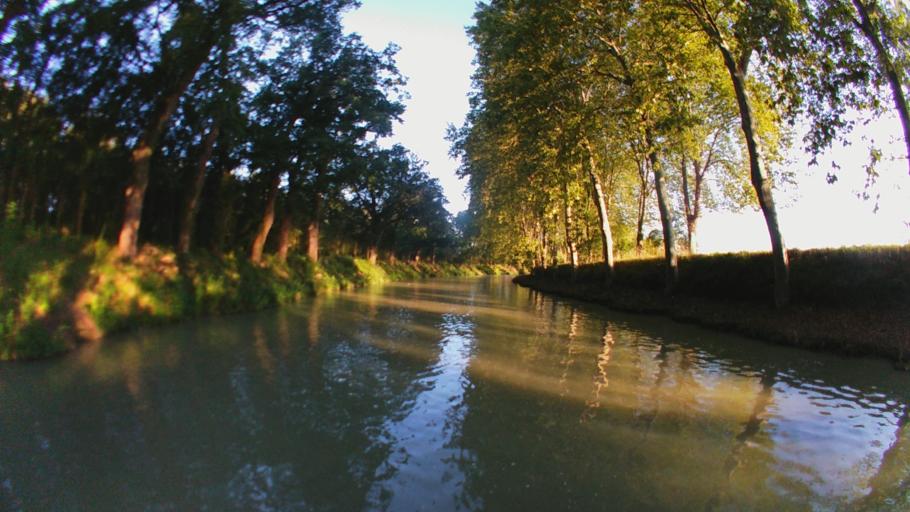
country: FR
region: Midi-Pyrenees
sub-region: Departement de la Haute-Garonne
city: Villenouvelle
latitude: 43.4115
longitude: 1.6488
